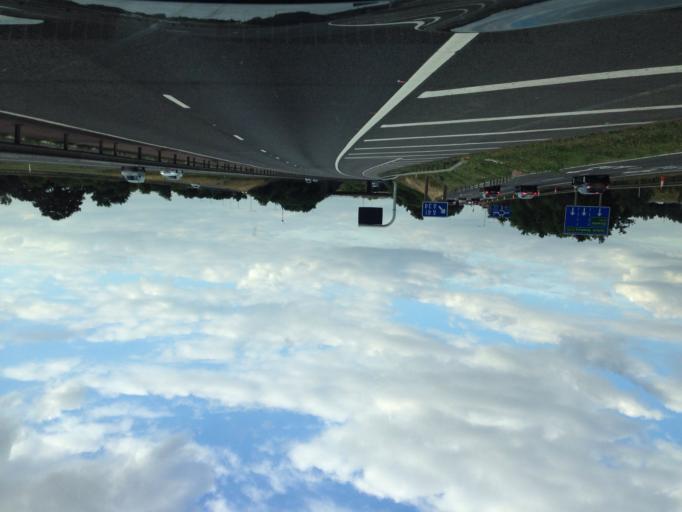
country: GB
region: England
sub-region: Oxfordshire
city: Bicester
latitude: 51.8722
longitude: -1.2003
